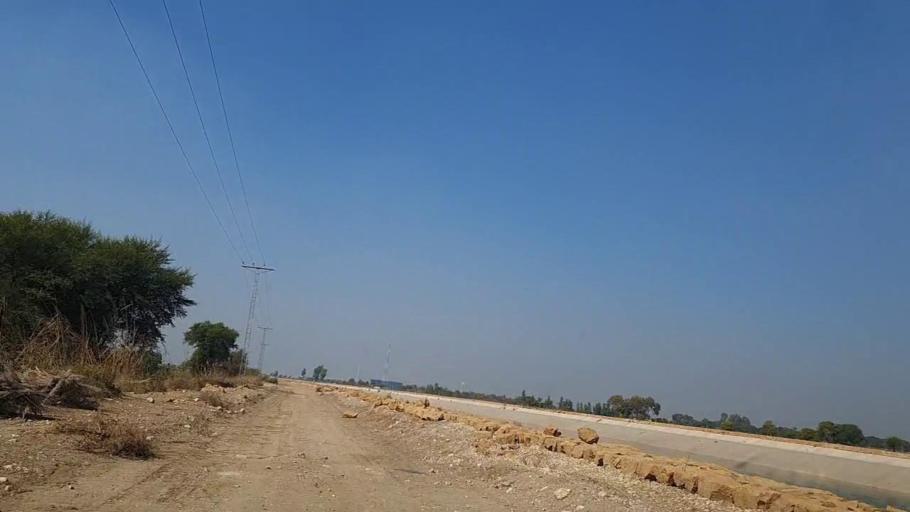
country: PK
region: Sindh
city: Sakrand
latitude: 26.2400
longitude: 68.2748
